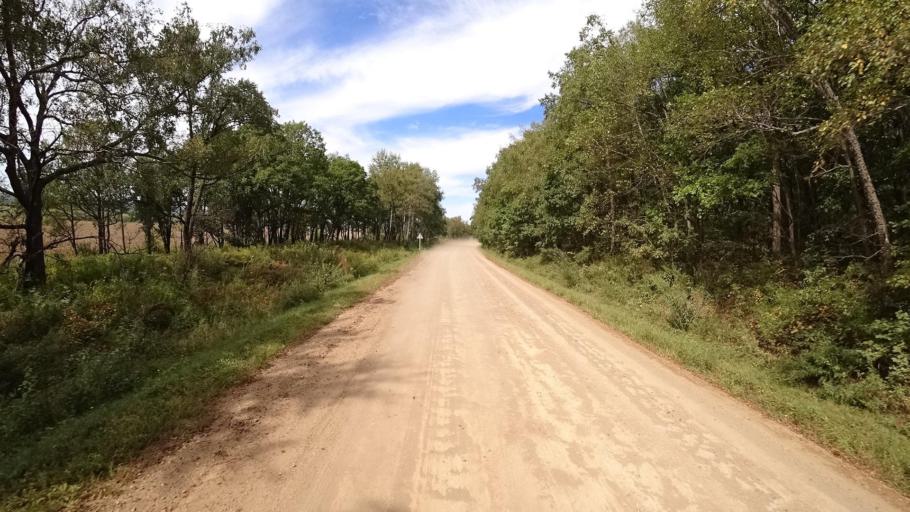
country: RU
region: Primorskiy
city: Yakovlevka
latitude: 44.5704
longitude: 133.5939
